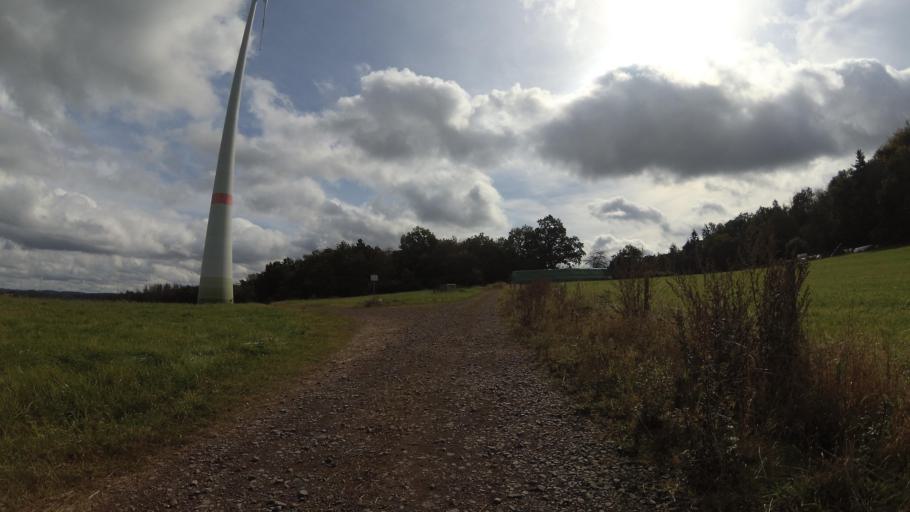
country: DE
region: Saarland
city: Namborn
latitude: 49.5449
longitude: 7.1638
